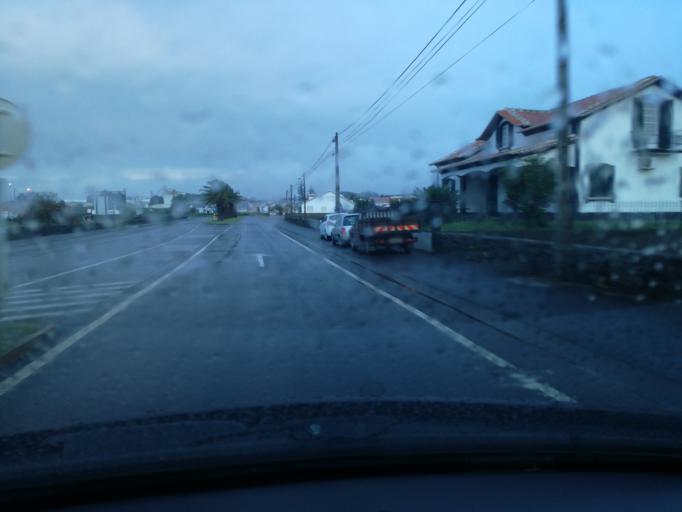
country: PT
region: Azores
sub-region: Praia da Vitoria
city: Praia da Vitoria
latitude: 38.7128
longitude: -27.0625
